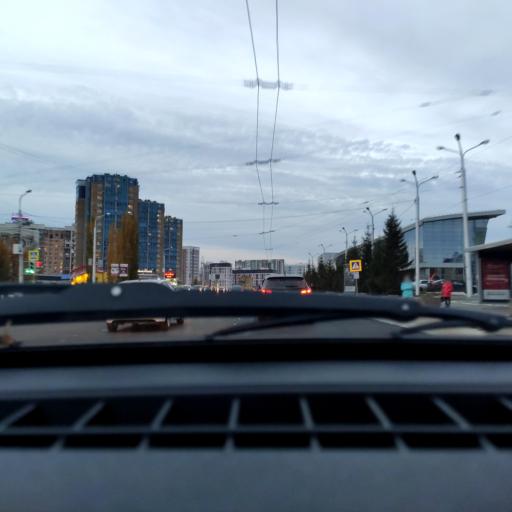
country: RU
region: Bashkortostan
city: Ufa
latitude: 54.7504
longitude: 56.0312
